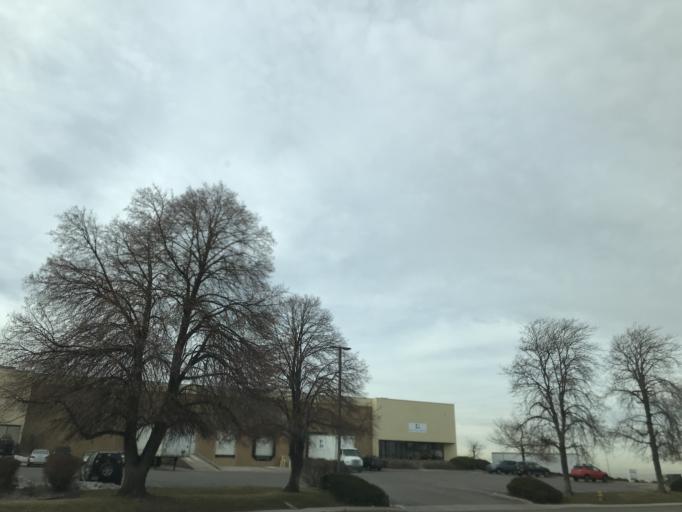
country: US
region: Colorado
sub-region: Adams County
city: Commerce City
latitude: 39.7832
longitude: -104.9175
